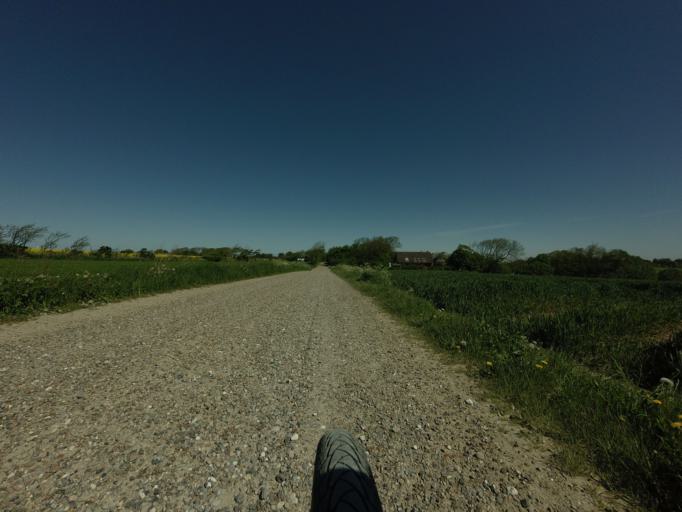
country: DK
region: North Denmark
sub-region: Hjorring Kommune
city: Hjorring
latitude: 57.4495
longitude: 9.8985
